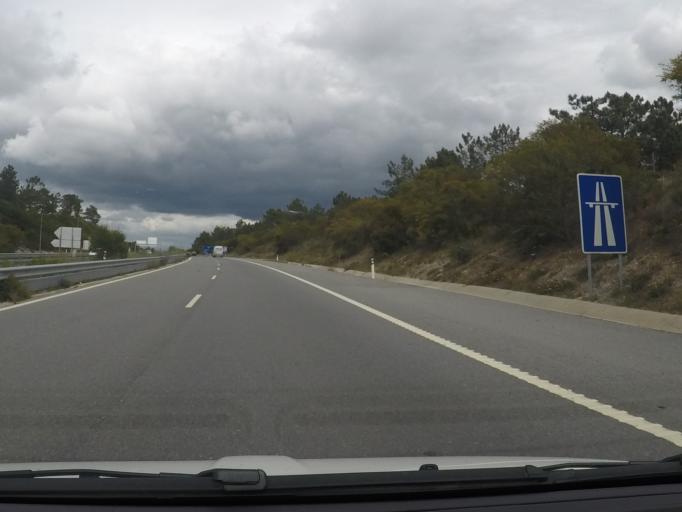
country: PT
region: Setubal
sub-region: Sines
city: Sines
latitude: 37.9748
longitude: -8.8059
